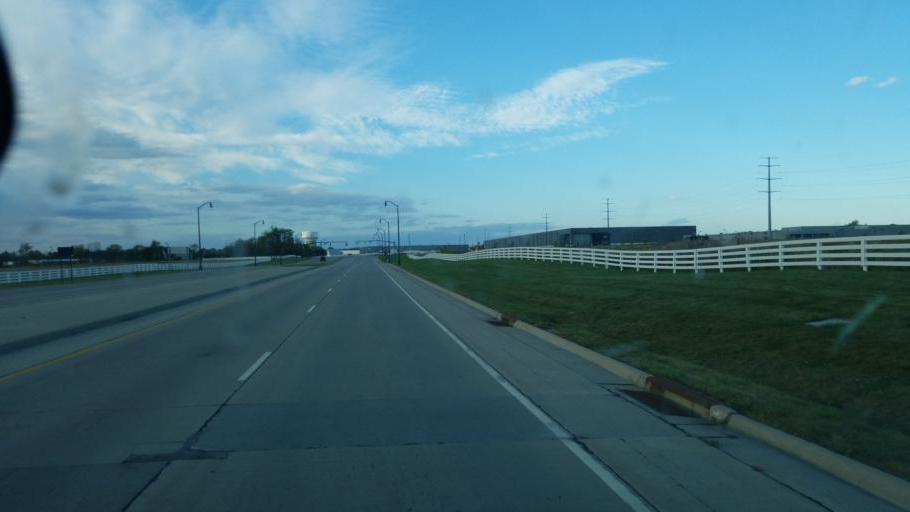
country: US
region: Ohio
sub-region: Franklin County
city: New Albany
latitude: 40.0820
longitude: -82.7531
